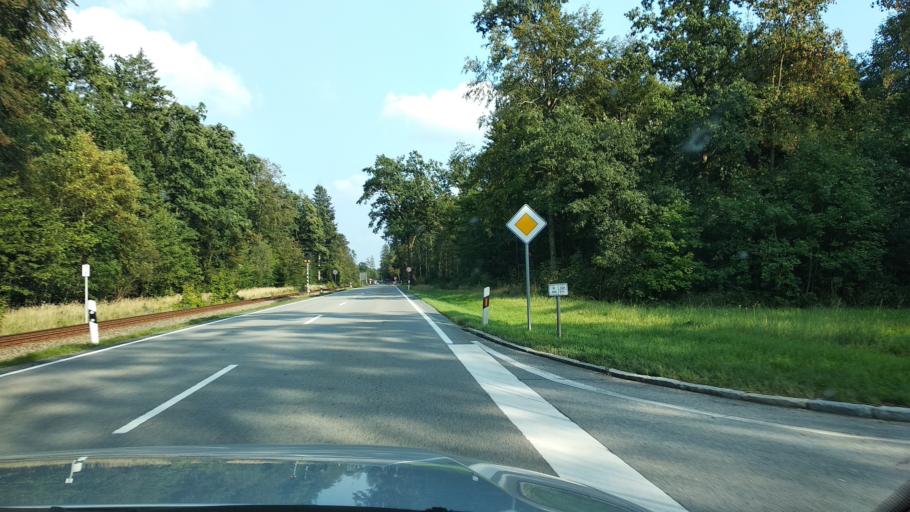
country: DE
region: Bavaria
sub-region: Upper Bavaria
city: Pfaffing
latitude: 48.0785
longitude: 12.1024
